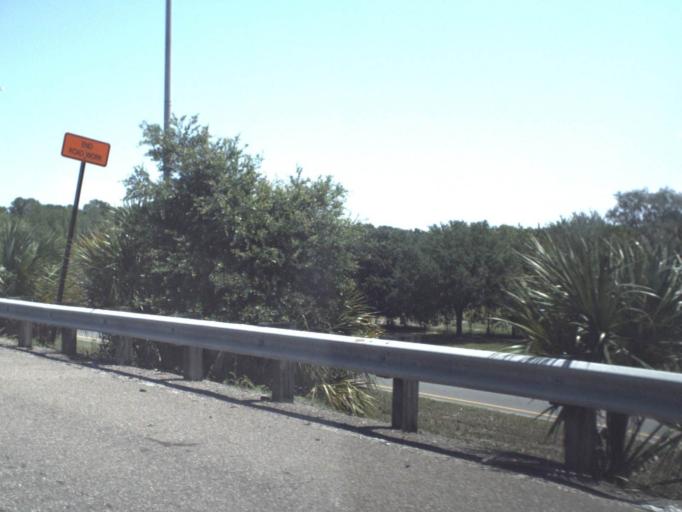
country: US
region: Florida
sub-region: Duval County
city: Jacksonville
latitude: 30.4128
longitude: -81.5646
